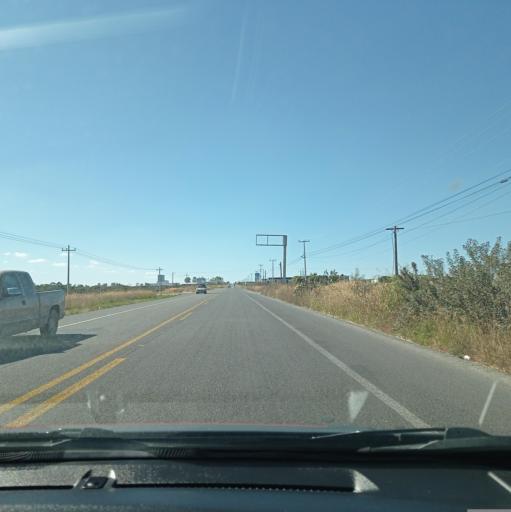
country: MX
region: Jalisco
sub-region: San Julian
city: Colonia Veintitres de Mayo
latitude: 21.0124
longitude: -102.2020
